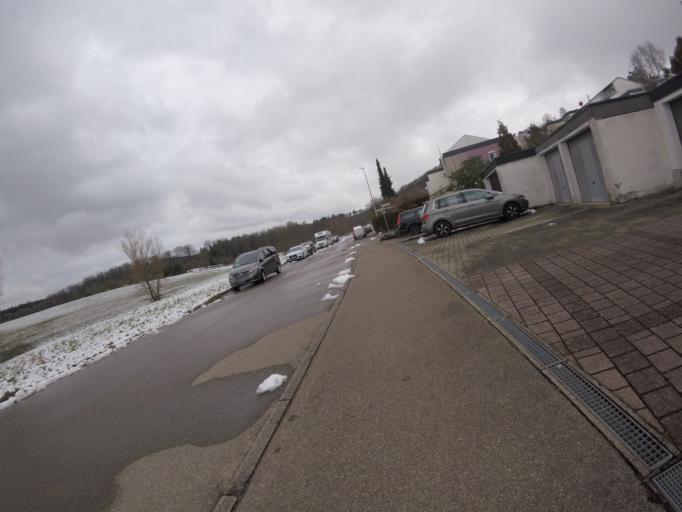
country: DE
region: Baden-Wuerttemberg
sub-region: Regierungsbezirk Stuttgart
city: Oberstenfeld
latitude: 48.9937
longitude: 9.3522
